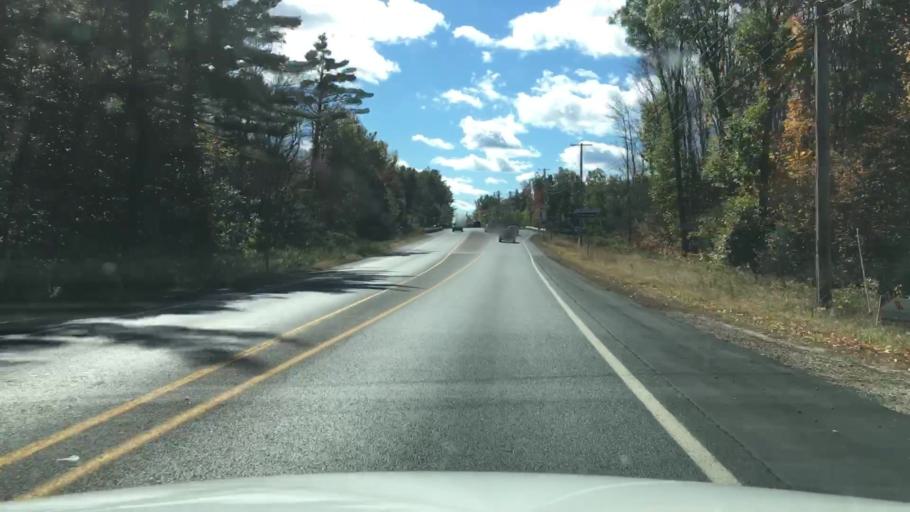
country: US
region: Maine
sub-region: York County
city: South Sanford
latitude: 43.4178
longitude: -70.7388
